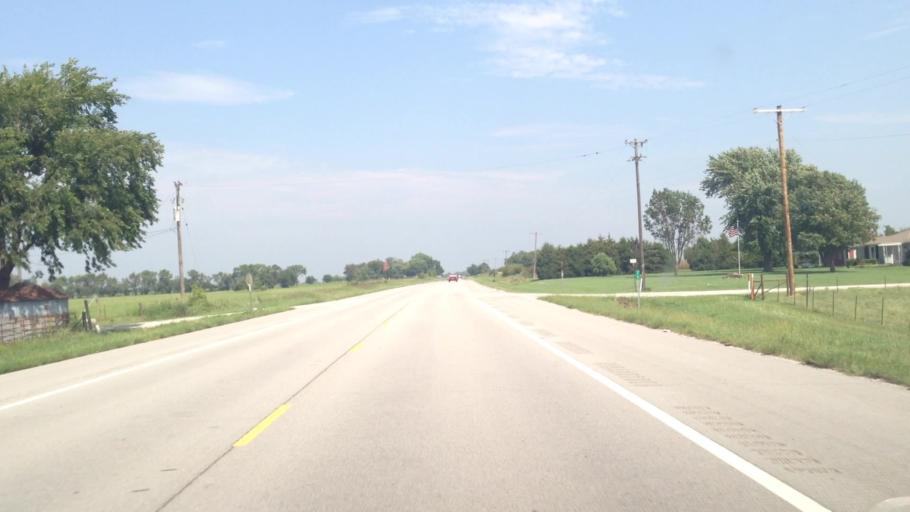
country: US
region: Kansas
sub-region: Labette County
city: Altamont
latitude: 37.2365
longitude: -95.2672
